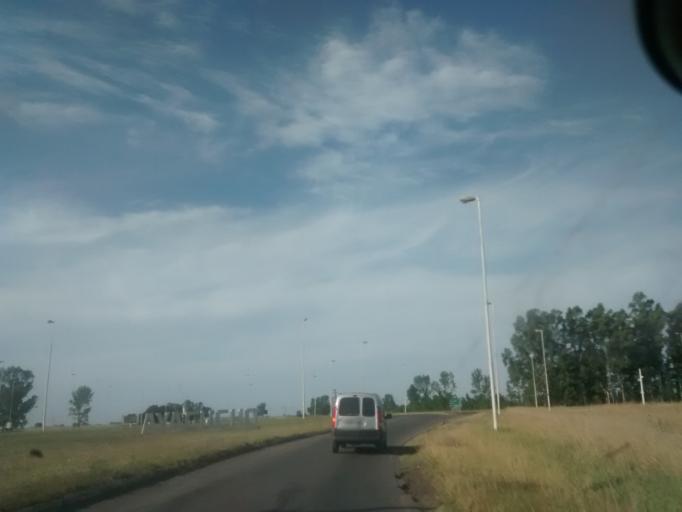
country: AR
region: Buenos Aires
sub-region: Partido de Ayacucho
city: Ayacucho
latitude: -37.1282
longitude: -58.5514
